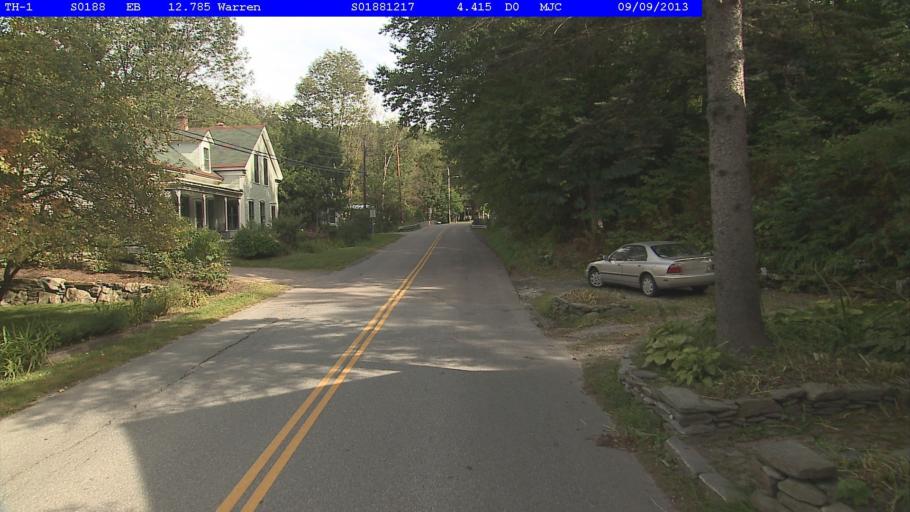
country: US
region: Vermont
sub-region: Washington County
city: Northfield
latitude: 44.1143
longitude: -72.8529
